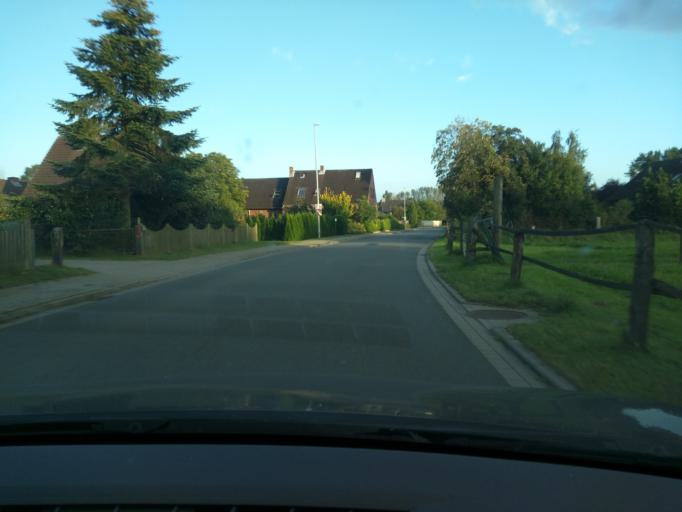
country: DE
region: Lower Saxony
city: Artlenburg
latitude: 53.3854
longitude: 10.4573
